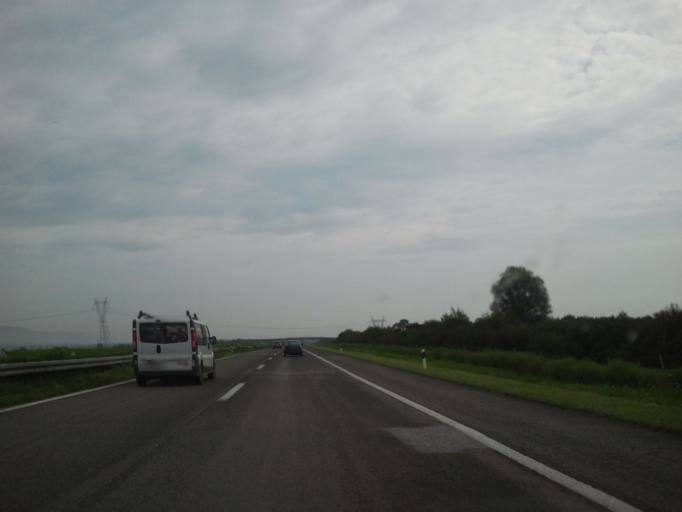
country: HR
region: Zagrebacka
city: Jastrebarsko
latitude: 45.6195
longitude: 15.6492
